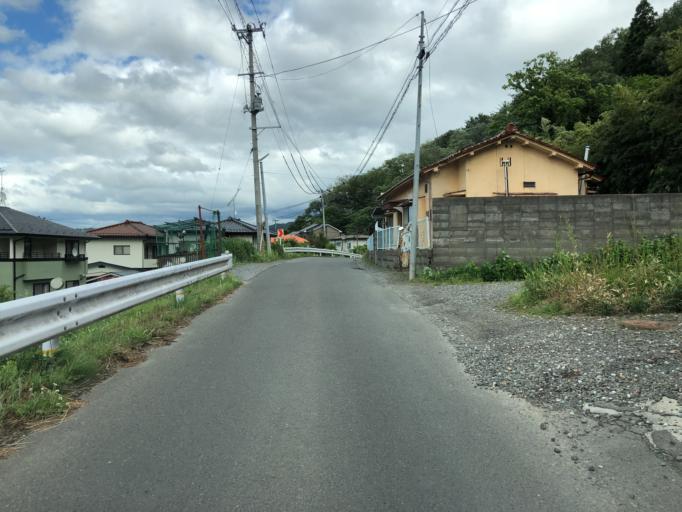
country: JP
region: Fukushima
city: Fukushima-shi
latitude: 37.7793
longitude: 140.4784
